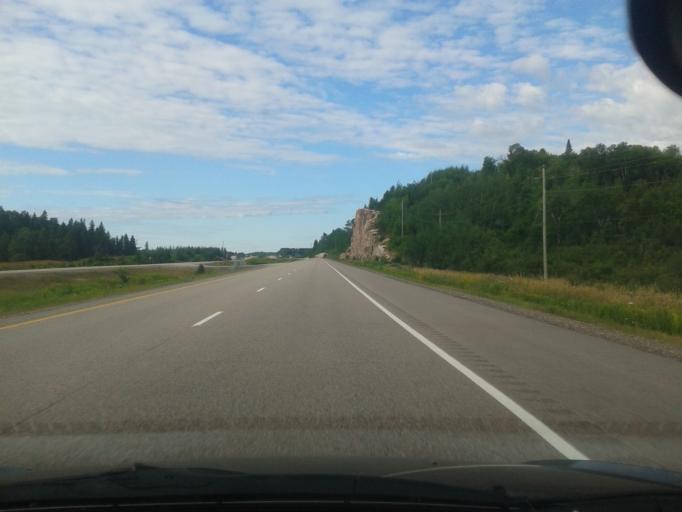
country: CA
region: Ontario
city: Powassan
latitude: 46.0185
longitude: -79.3449
